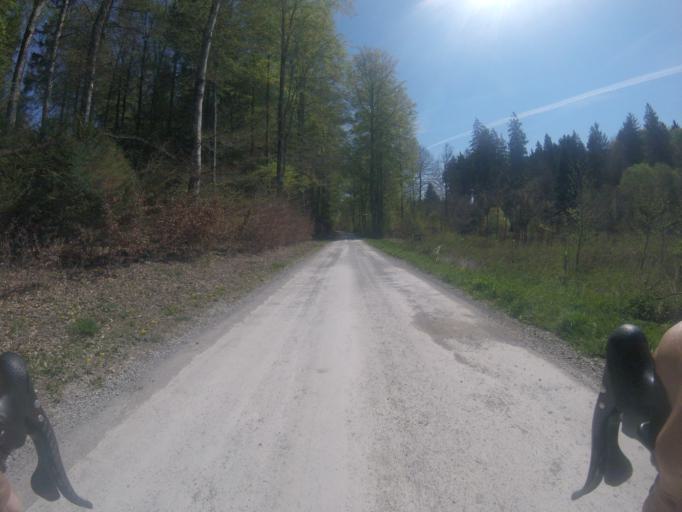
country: CH
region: Fribourg
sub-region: Sense District
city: Flamatt
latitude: 46.9118
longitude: 7.3089
